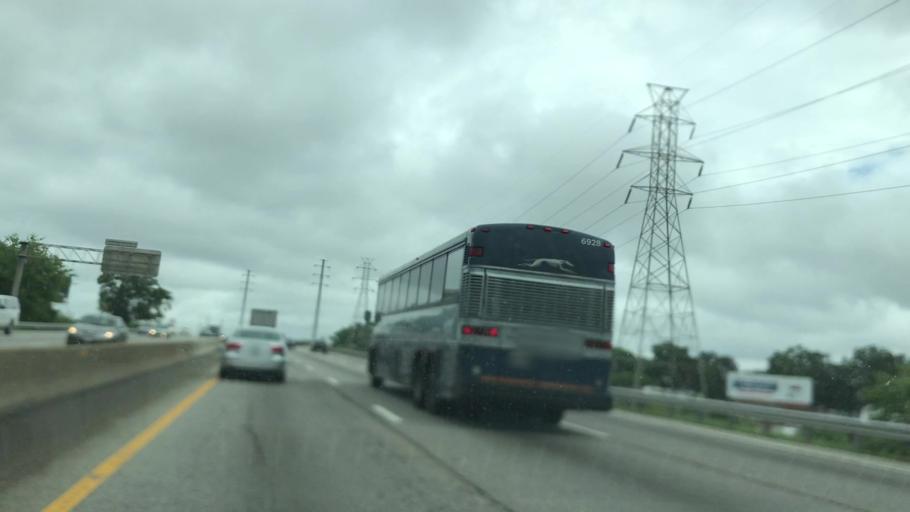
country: US
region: Virginia
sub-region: City of Richmond
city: Richmond
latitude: 37.5569
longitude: -77.4495
